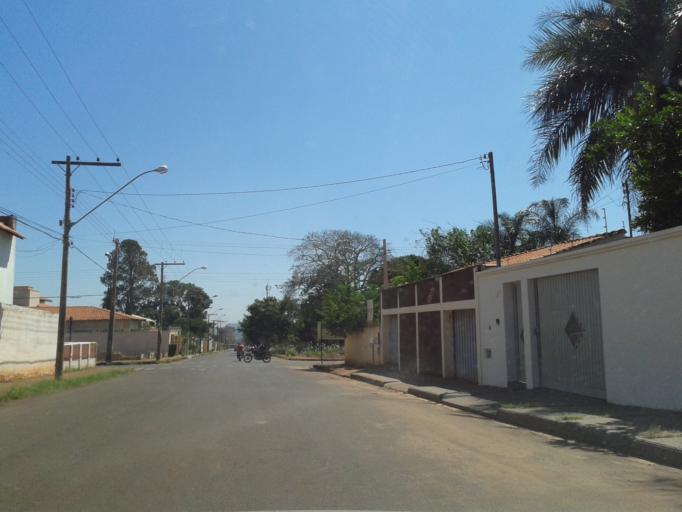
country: BR
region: Minas Gerais
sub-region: Ituiutaba
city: Ituiutaba
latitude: -18.9905
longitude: -49.4571
